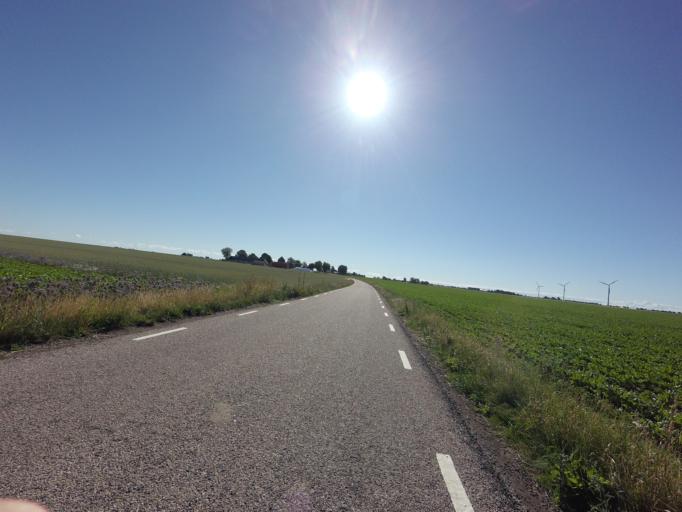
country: SE
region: Skane
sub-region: Trelleborgs Kommun
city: Skare
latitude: 55.3945
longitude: 13.0339
